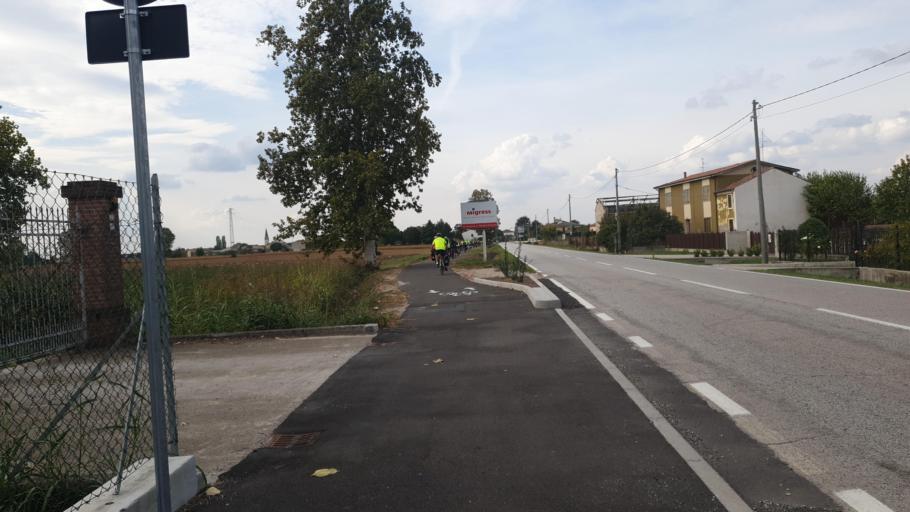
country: IT
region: Veneto
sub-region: Provincia di Vicenza
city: Poiana Maggiore
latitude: 45.2880
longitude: 11.5149
